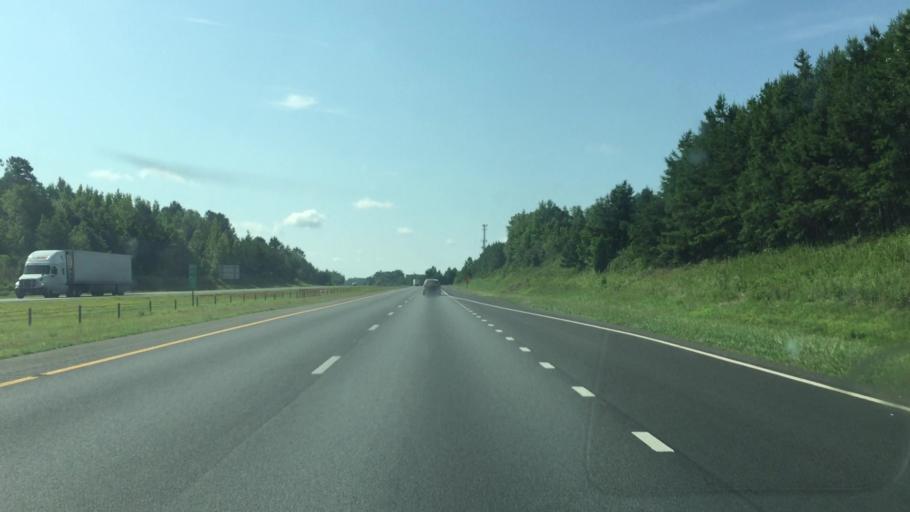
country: US
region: North Carolina
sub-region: Mecklenburg County
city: Mint Hill
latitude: 35.2181
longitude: -80.6483
